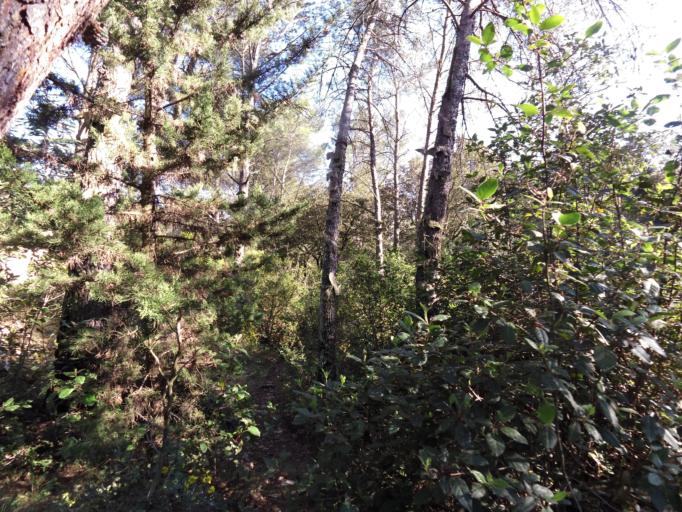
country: FR
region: Languedoc-Roussillon
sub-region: Departement du Gard
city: Congenies
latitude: 43.7841
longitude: 4.1564
